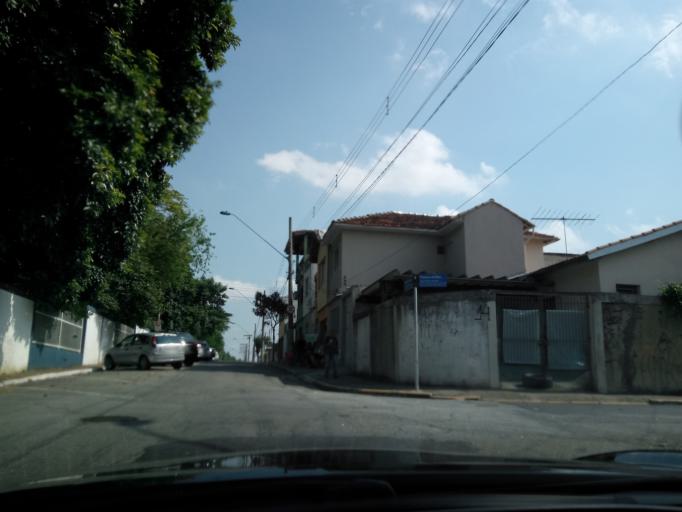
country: BR
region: Sao Paulo
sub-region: Sao Caetano Do Sul
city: Sao Caetano do Sul
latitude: -23.6312
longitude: -46.5743
